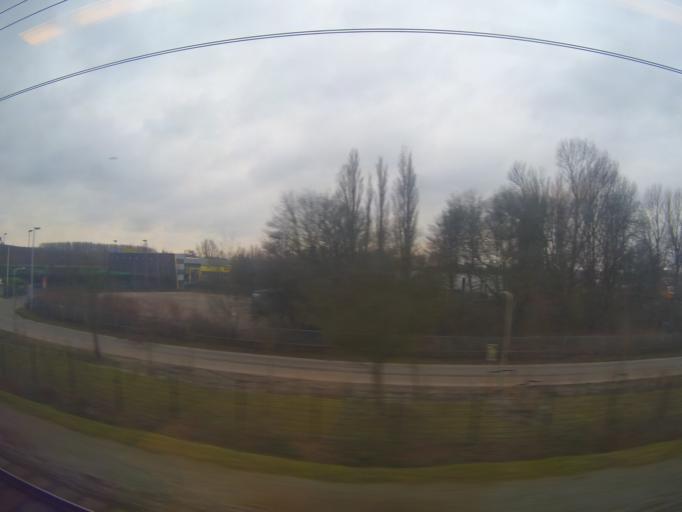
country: NL
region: South Holland
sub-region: Gemeente Leidschendam-Voorburg
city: Voorburg
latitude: 52.0630
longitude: 4.3699
